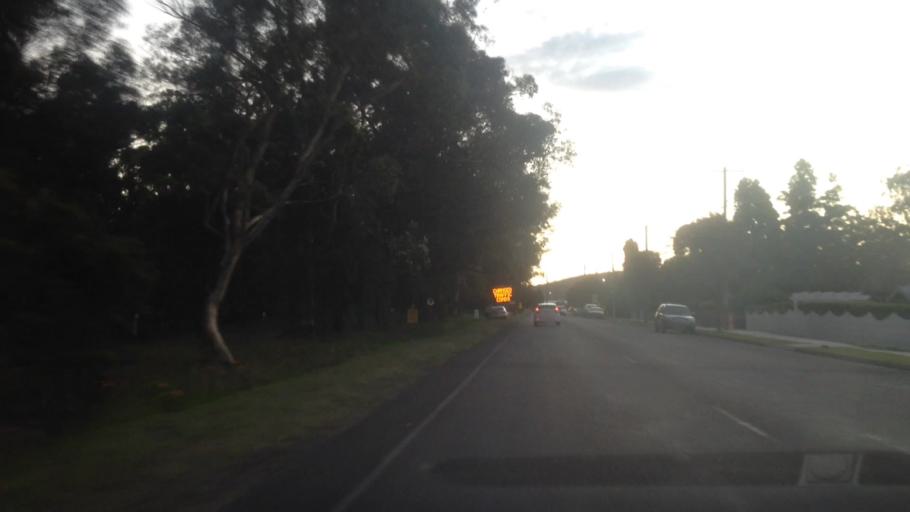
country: AU
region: New South Wales
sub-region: Lake Macquarie Shire
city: Cooranbong
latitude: -33.0745
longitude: 151.4571
